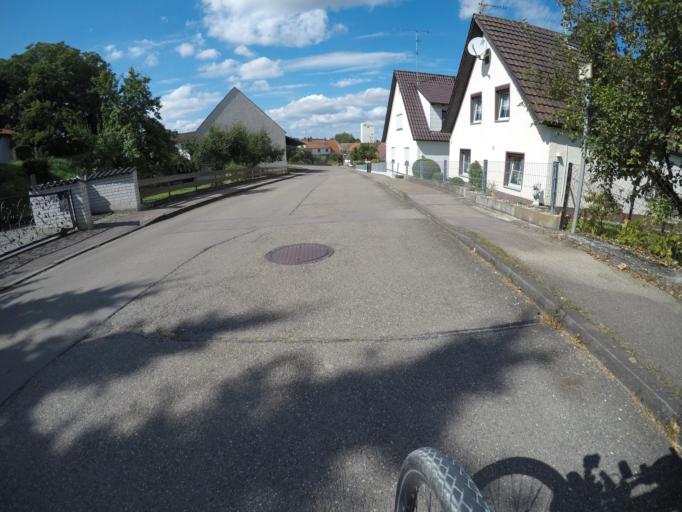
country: DE
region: Bavaria
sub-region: Swabia
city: Wittislingen
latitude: 48.6157
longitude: 10.4177
